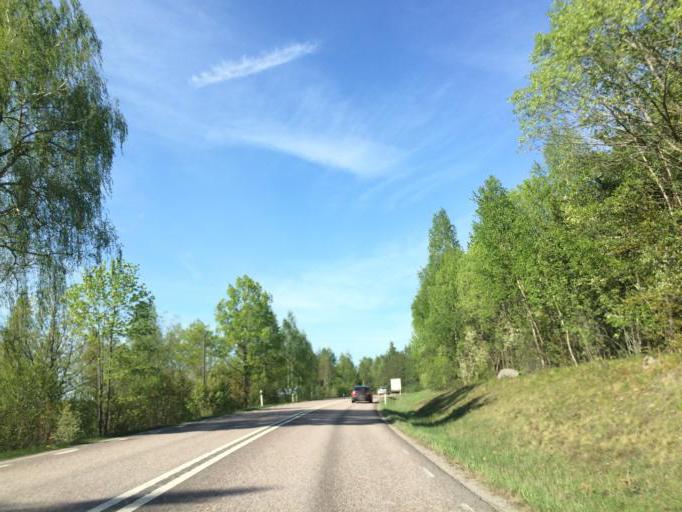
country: SE
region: Soedermanland
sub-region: Katrineholms Kommun
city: Katrineholm
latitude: 59.1449
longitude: 16.1176
